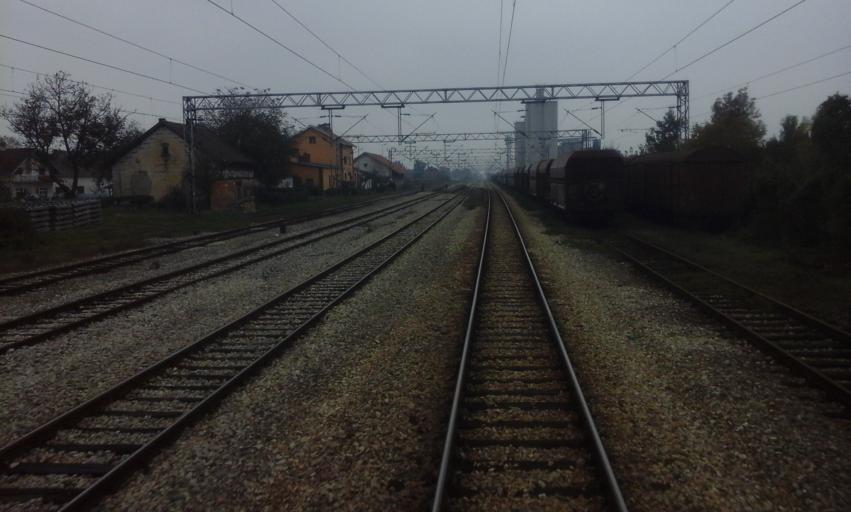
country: RS
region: Central Serbia
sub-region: Sumadijski Okrug
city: Lapovo
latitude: 44.2406
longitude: 21.0965
